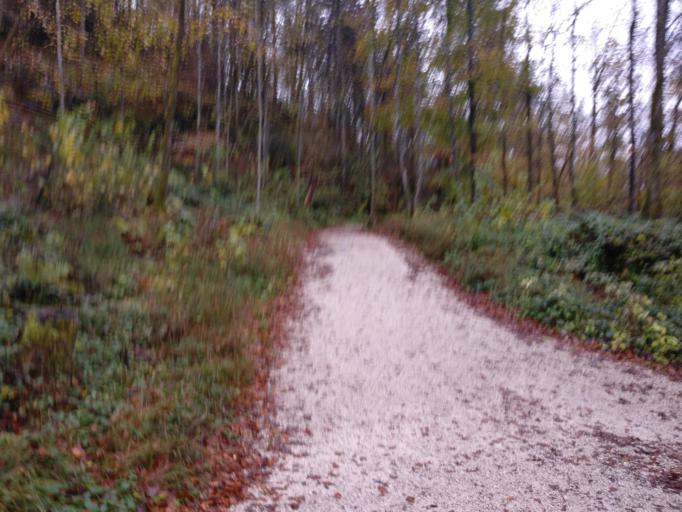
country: DE
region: Bavaria
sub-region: Upper Bavaria
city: Schoenau am Koenigssee
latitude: 47.5844
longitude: 12.9909
